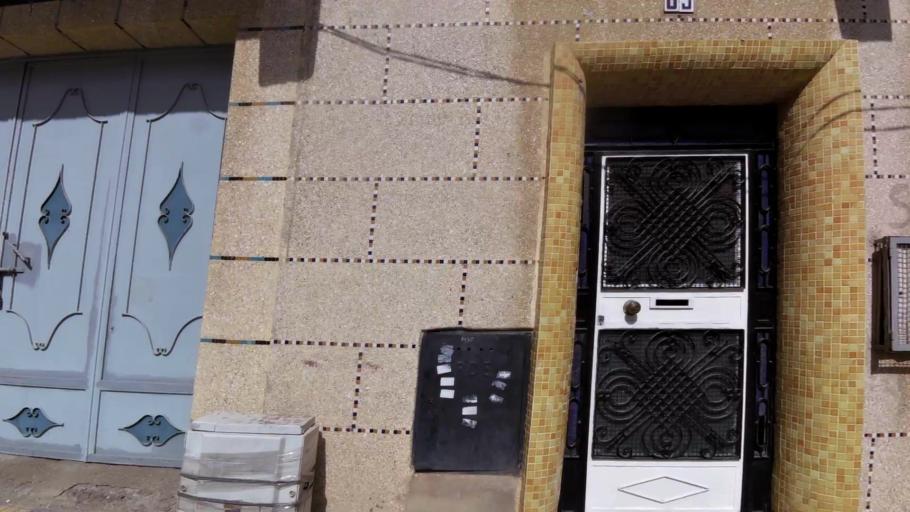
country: MA
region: Tanger-Tetouan
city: Tetouan
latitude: 35.5851
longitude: -5.3507
